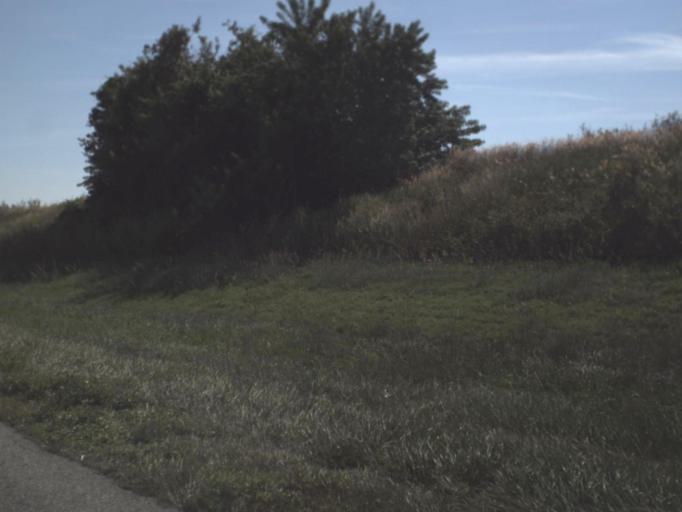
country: US
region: Florida
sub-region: Highlands County
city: Lake Placid
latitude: 27.2580
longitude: -81.3433
